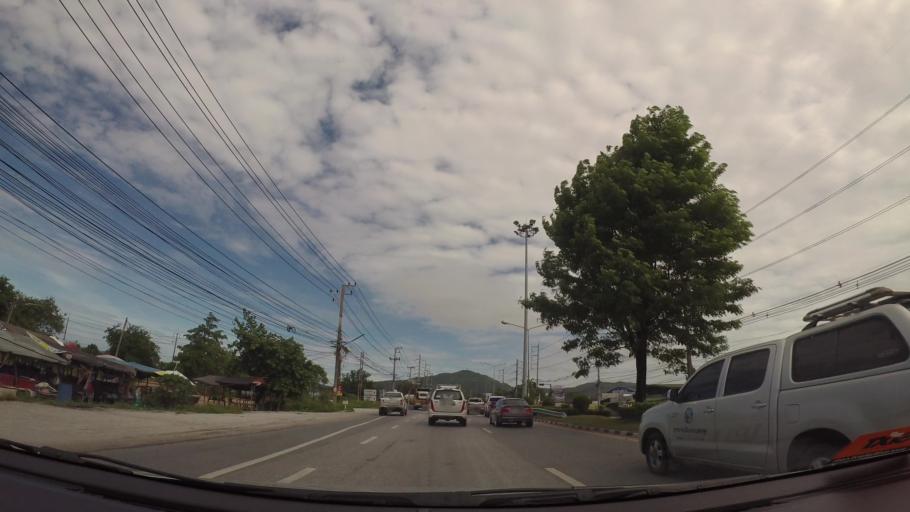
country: TH
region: Rayong
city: Ban Chang
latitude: 12.7396
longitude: 101.1232
